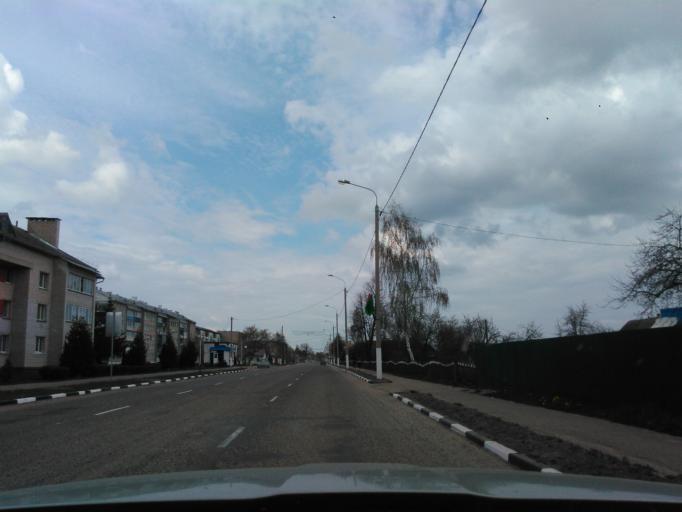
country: BY
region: Vitebsk
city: Chashniki
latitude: 54.8480
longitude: 29.1733
